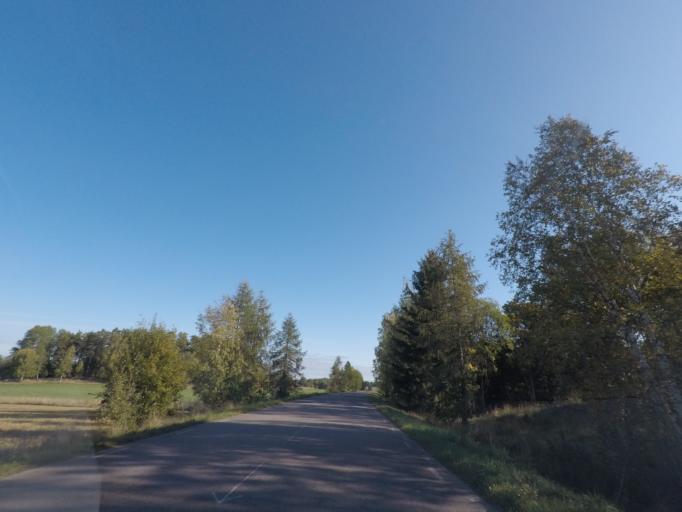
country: SE
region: Soedermanland
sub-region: Eskilstuna Kommun
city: Kvicksund
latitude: 59.5454
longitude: 16.4005
